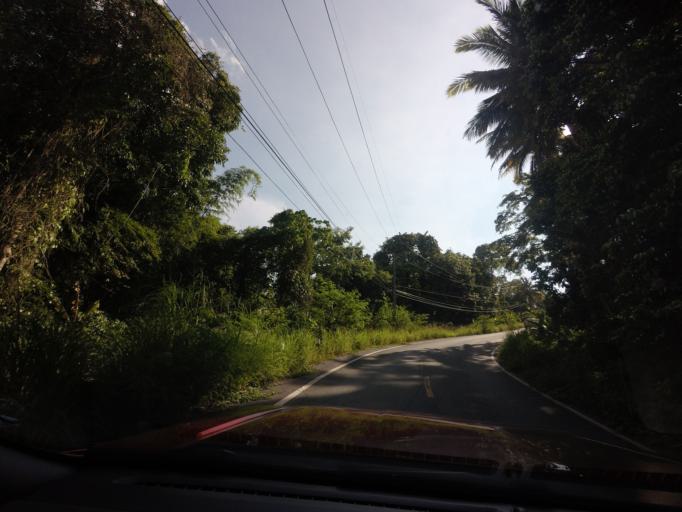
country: TH
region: Yala
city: Than To
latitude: 6.0701
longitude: 101.3503
